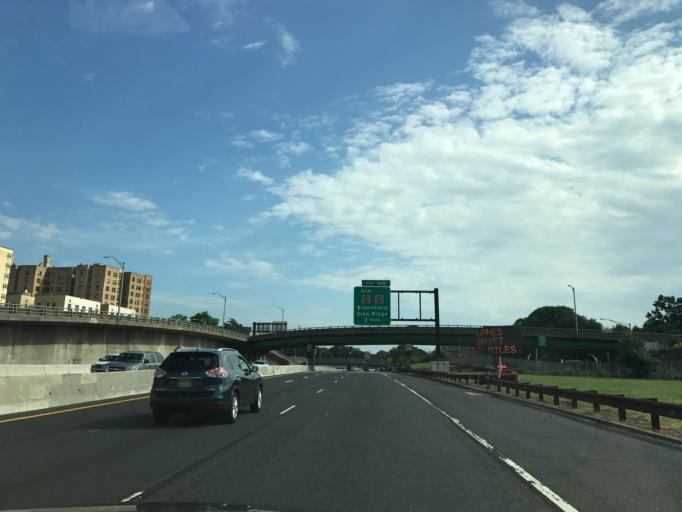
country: US
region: New Jersey
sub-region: Essex County
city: East Orange
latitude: 40.7547
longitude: -74.2102
